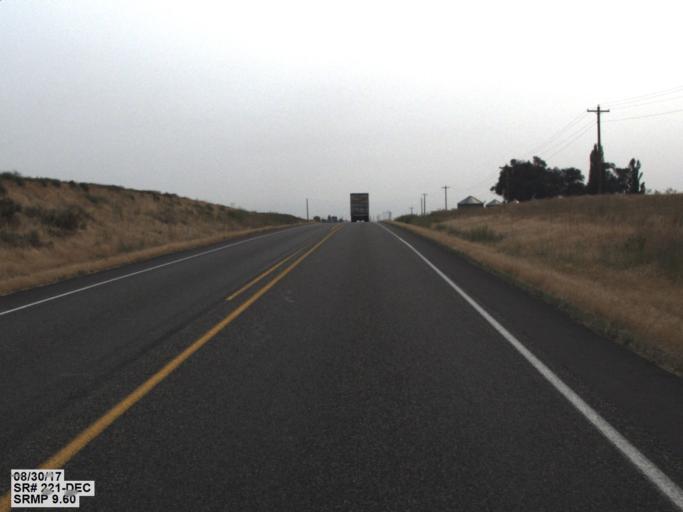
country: US
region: Oregon
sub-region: Morrow County
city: Irrigon
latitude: 46.0742
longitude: -119.6021
